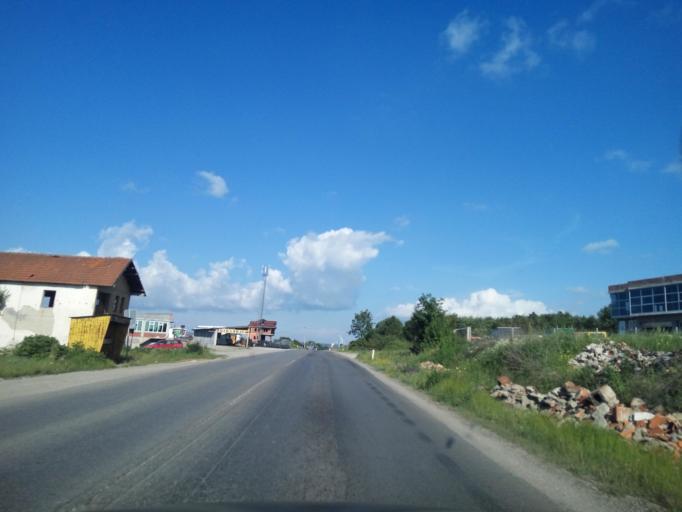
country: XK
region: Prizren
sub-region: Komuna e Malisheves
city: Llazice
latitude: 42.5872
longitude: 20.6789
